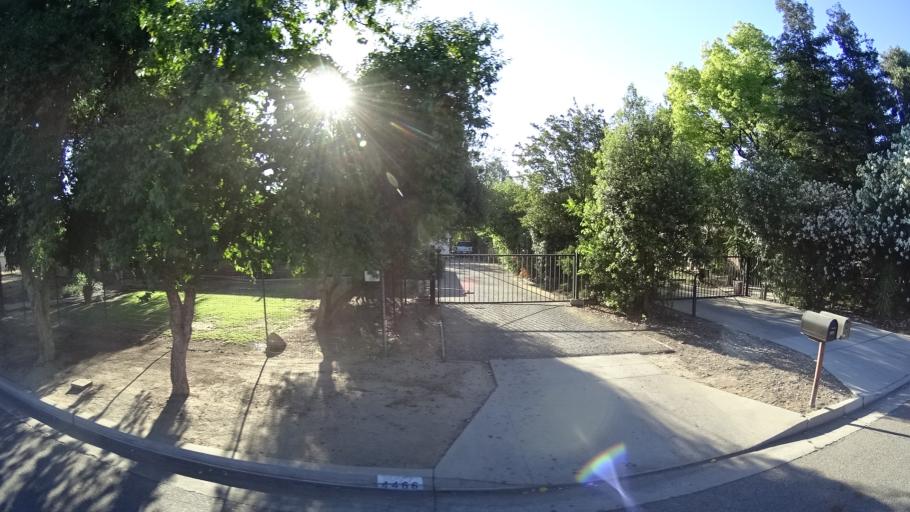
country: US
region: California
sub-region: Fresno County
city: Fresno
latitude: 36.7985
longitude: -119.8220
